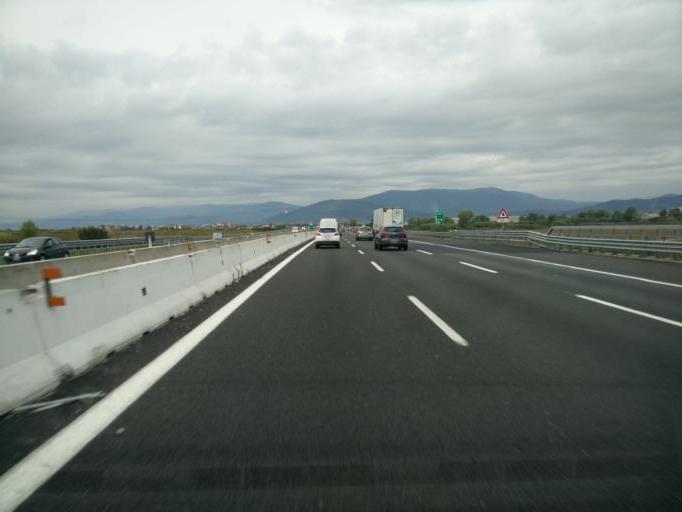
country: IT
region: Tuscany
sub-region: Province of Florence
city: San Donnino
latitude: 43.8026
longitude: 11.1544
